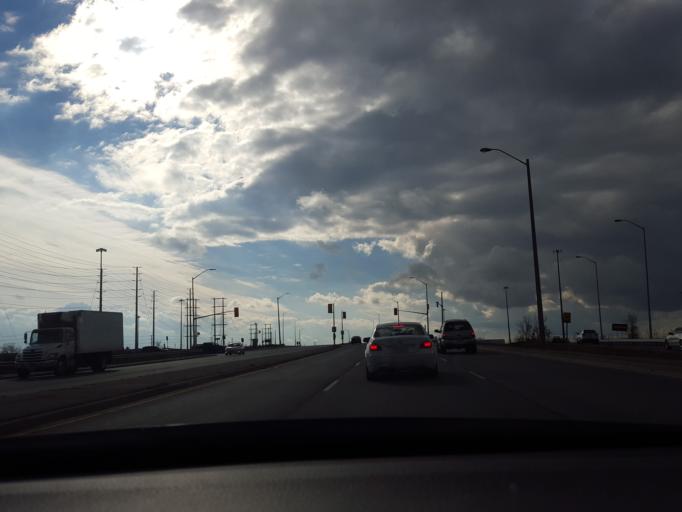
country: CA
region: Ontario
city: Brampton
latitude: 43.6635
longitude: -79.6877
